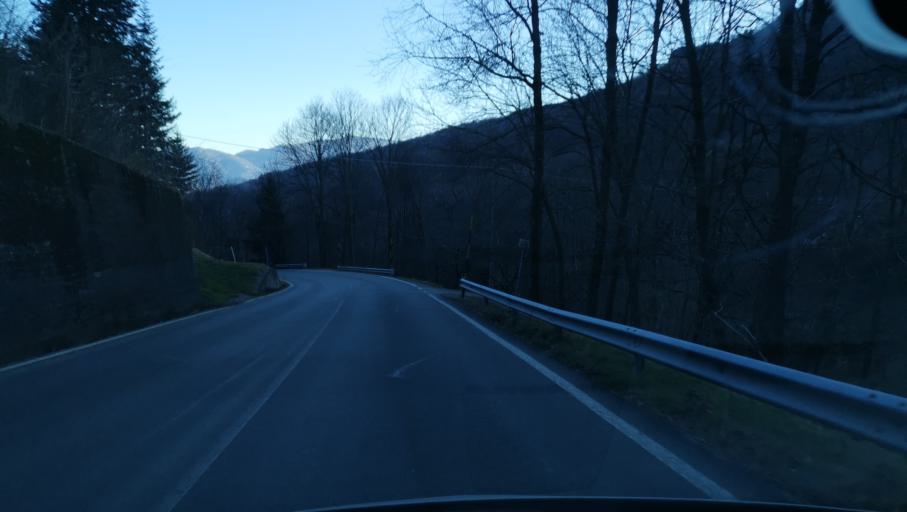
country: IT
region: Piedmont
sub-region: Provincia di Torino
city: Lusernetta
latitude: 44.7527
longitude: 7.2608
